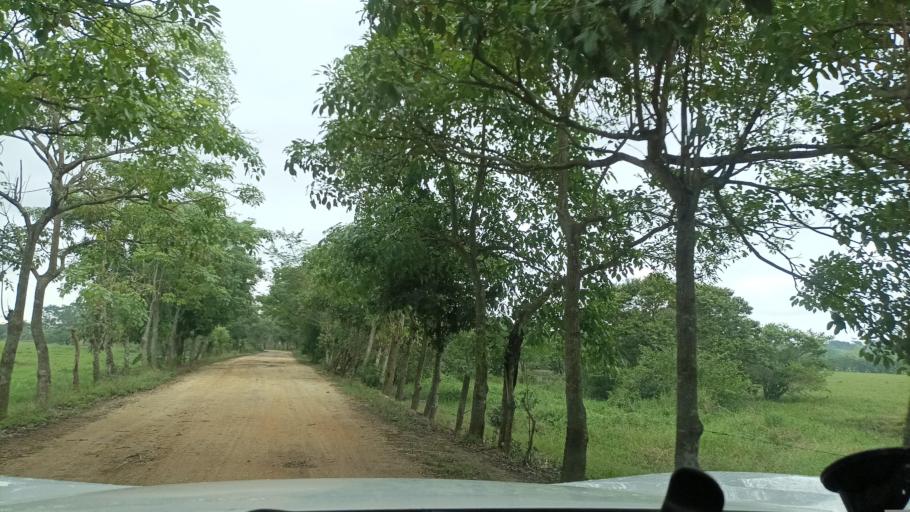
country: MX
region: Veracruz
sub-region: Moloacan
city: Cuichapa
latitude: 17.7791
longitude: -94.3883
